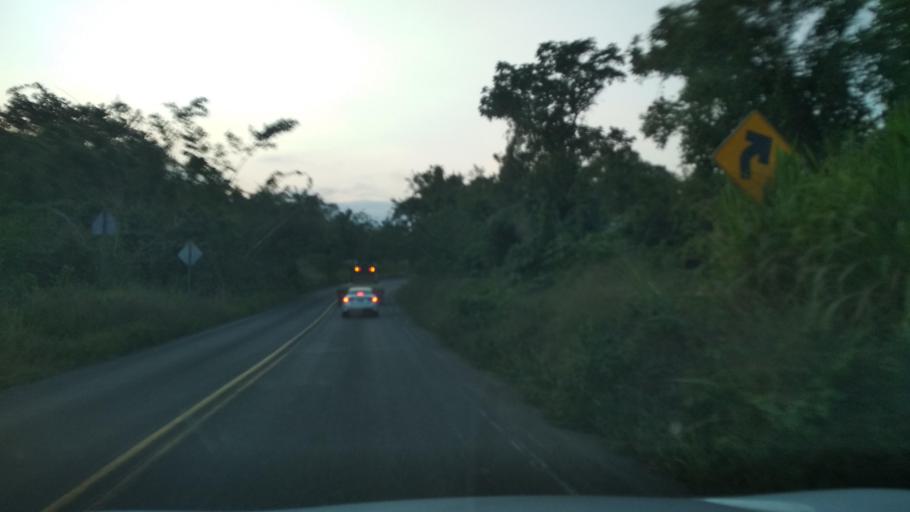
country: MX
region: Veracruz
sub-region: Poza Rica de Hidalgo
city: Arroyo del Maiz Uno
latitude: 20.4793
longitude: -97.3871
